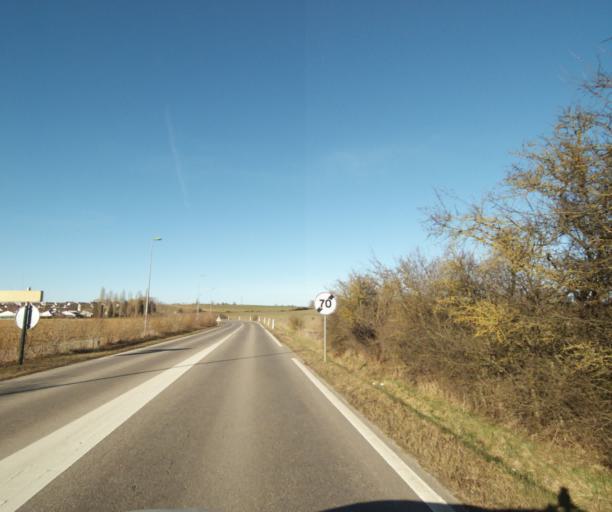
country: FR
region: Lorraine
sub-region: Departement de Meurthe-et-Moselle
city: Fleville-devant-Nancy
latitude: 48.6388
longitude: 6.2114
